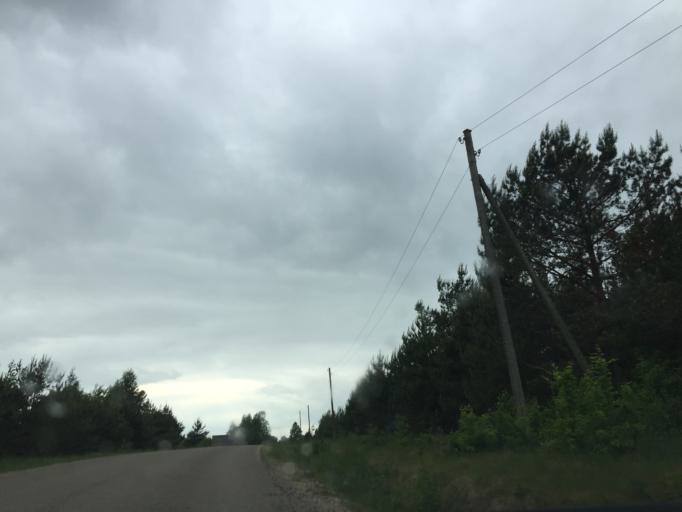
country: LV
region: Aglona
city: Aglona
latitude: 56.0614
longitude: 26.8316
